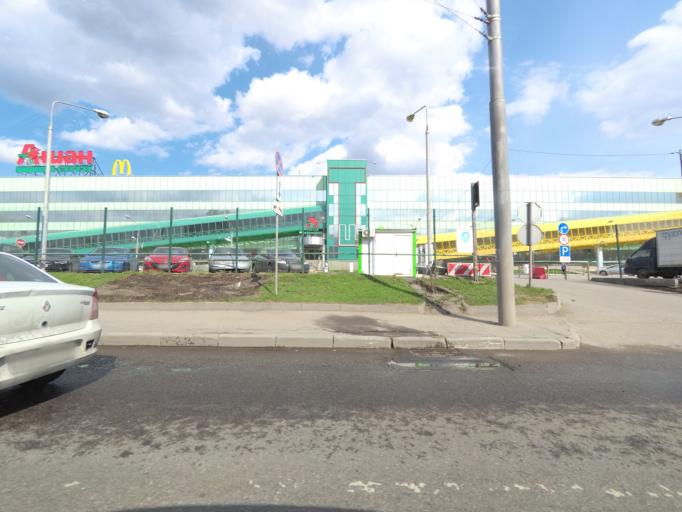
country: RU
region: Moscow
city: Gol'yanovo
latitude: 55.8081
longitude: 37.8296
